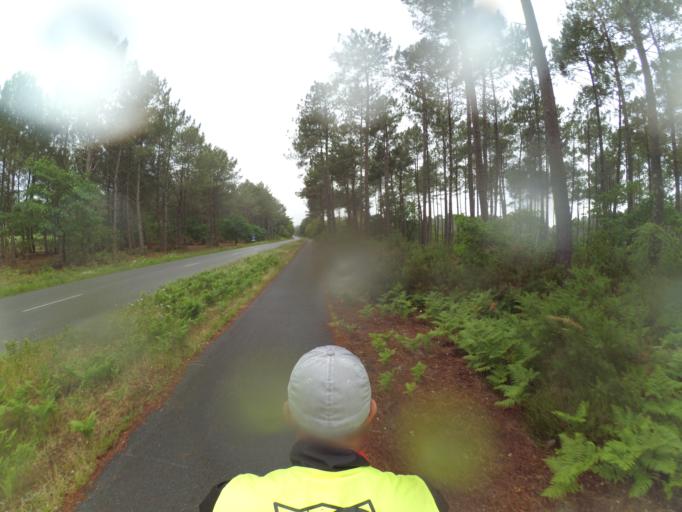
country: FR
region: Aquitaine
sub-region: Departement des Landes
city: Mimizan
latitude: 44.2387
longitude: -1.2113
